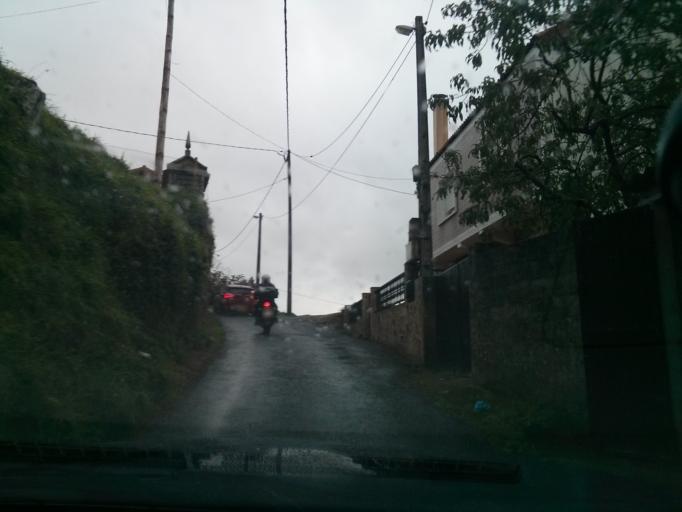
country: ES
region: Galicia
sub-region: Provincia da Coruna
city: Outes
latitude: 42.8390
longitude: -8.8582
